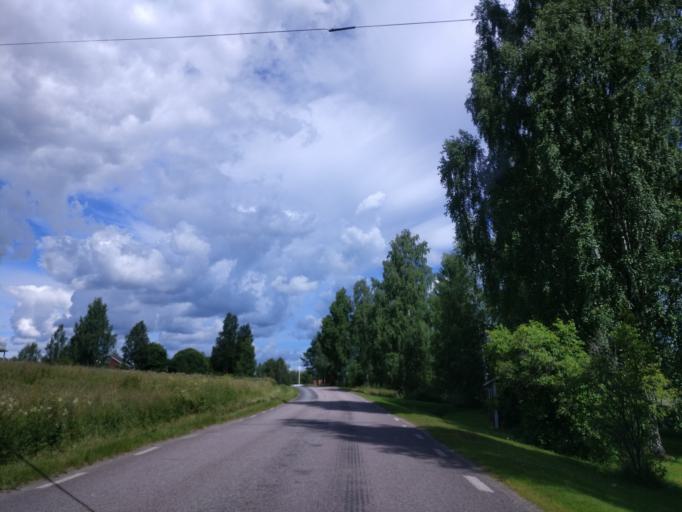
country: SE
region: Vaermland
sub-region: Hagfors Kommun
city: Ekshaerad
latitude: 60.1399
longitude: 13.4594
